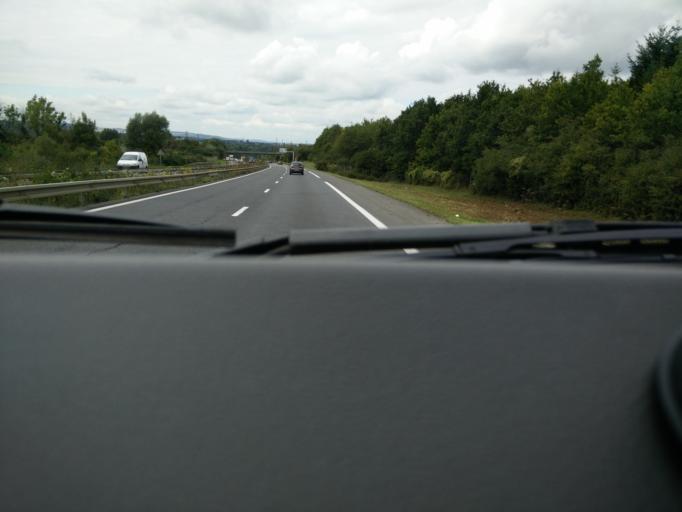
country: FR
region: Champagne-Ardenne
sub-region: Departement des Ardennes
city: Lumes
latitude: 49.7365
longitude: 4.7927
